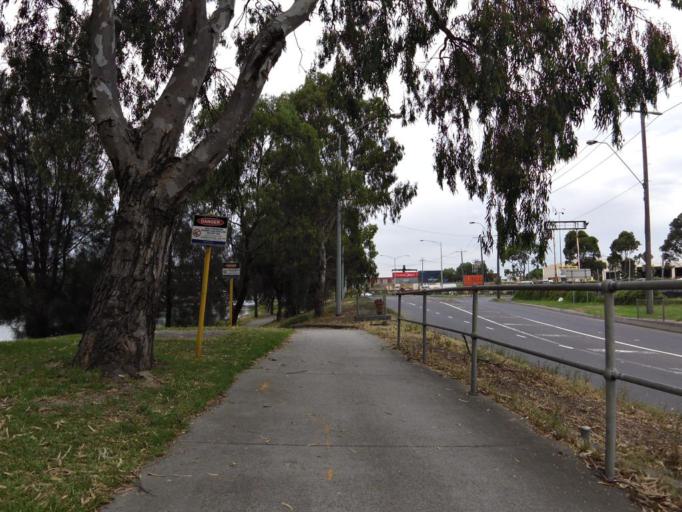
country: AU
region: Victoria
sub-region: Maribyrnong
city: Footscray
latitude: -37.8061
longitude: 144.9082
